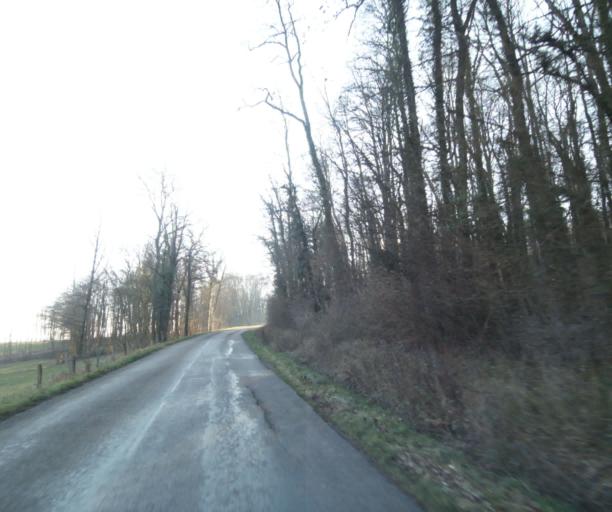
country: FR
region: Champagne-Ardenne
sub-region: Departement de la Haute-Marne
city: Bienville
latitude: 48.5748
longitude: 5.0803
